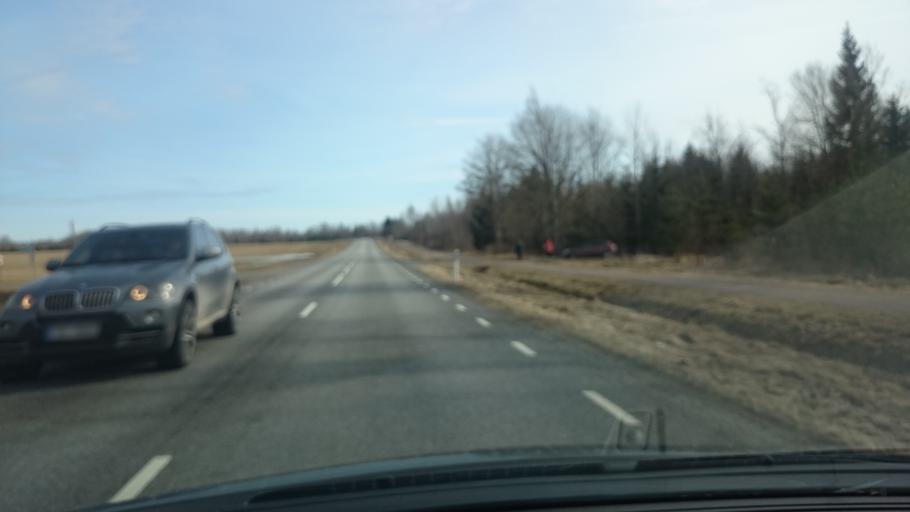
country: EE
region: Jaervamaa
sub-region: Paide linn
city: Paide
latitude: 58.8866
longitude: 25.5085
